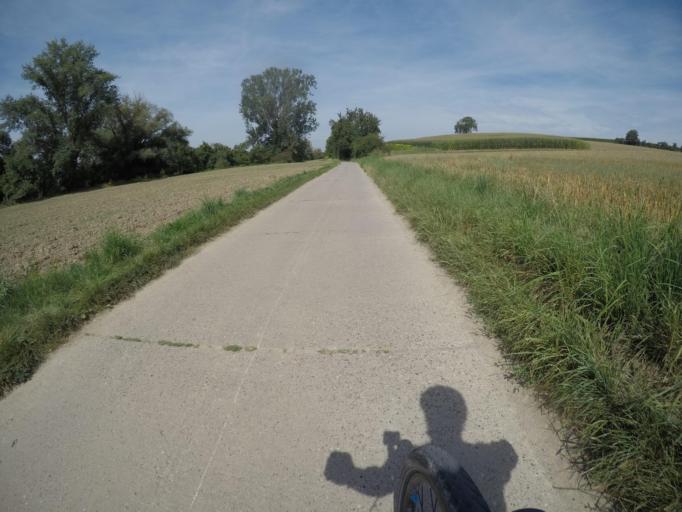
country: DE
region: Baden-Wuerttemberg
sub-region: Karlsruhe Region
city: Gondelsheim
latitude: 49.0501
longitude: 8.6706
